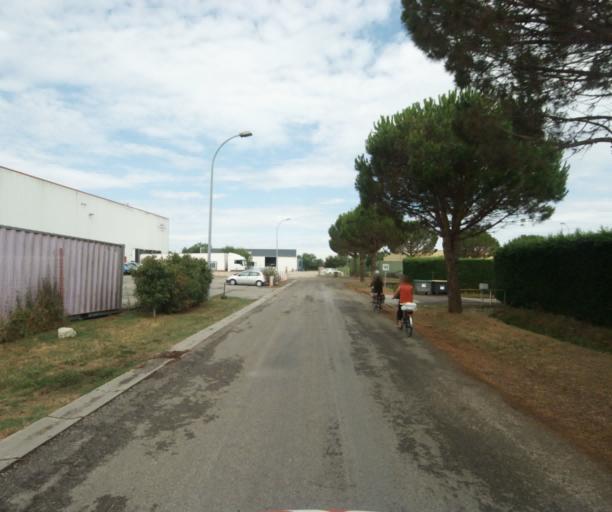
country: FR
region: Midi-Pyrenees
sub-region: Departement de la Haute-Garonne
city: Revel
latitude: 43.4575
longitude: 1.9788
